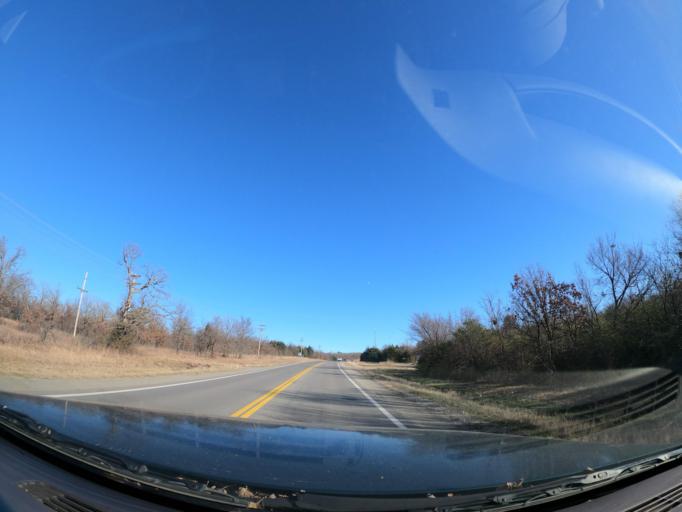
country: US
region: Oklahoma
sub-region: Pittsburg County
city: Longtown
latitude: 35.2389
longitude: -95.4732
